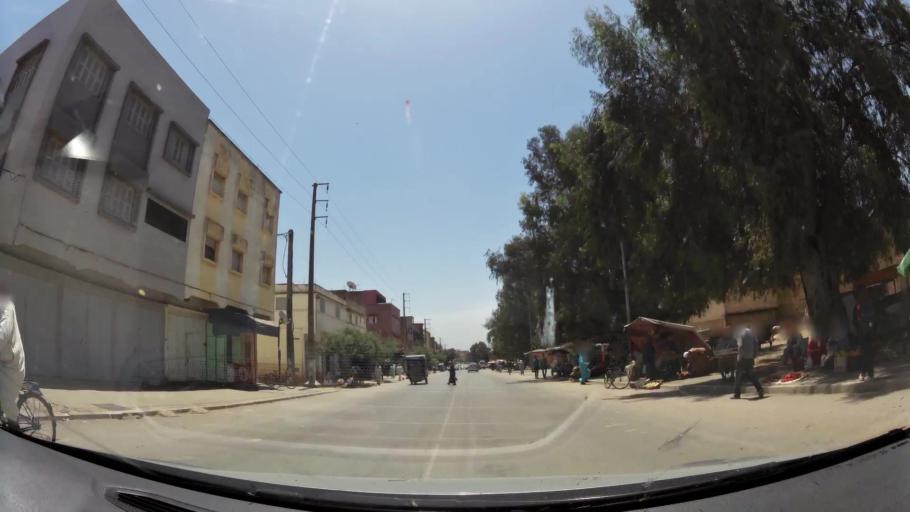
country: MA
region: Rabat-Sale-Zemmour-Zaer
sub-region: Khemisset
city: Khemisset
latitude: 33.8355
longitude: -6.0668
